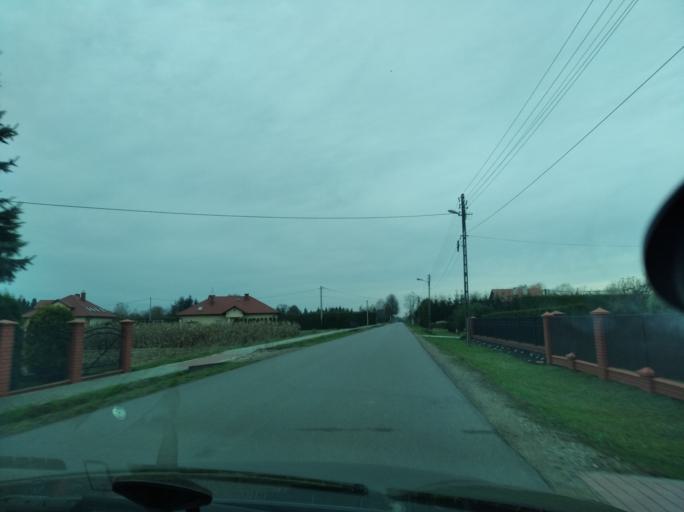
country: PL
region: Subcarpathian Voivodeship
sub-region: Powiat lancucki
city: Czarna
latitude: 50.0990
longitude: 22.2074
